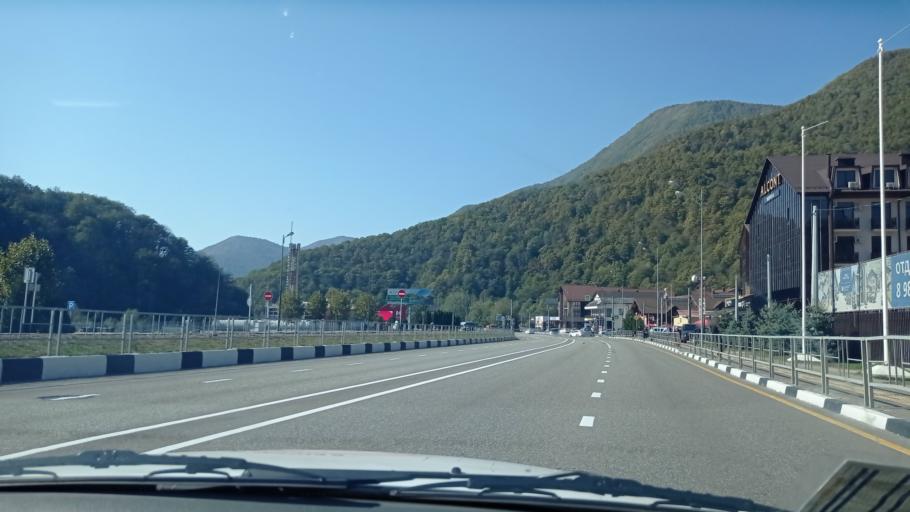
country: RU
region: Krasnodarskiy
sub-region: Sochi City
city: Krasnaya Polyana
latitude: 43.6860
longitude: 40.2529
